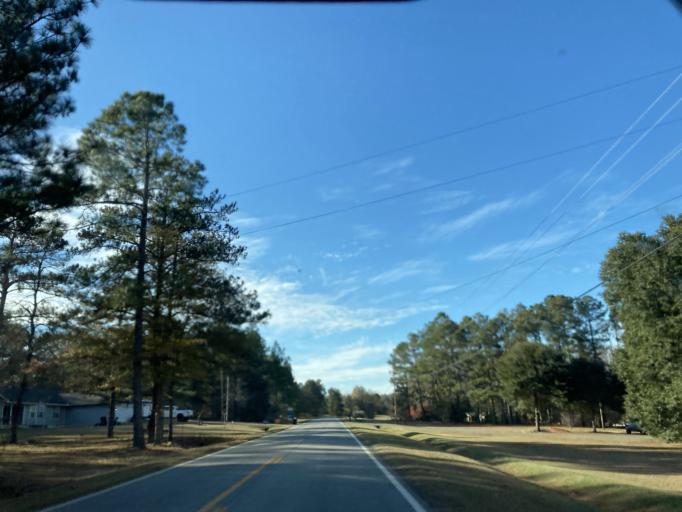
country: US
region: Georgia
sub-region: Jones County
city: Gray
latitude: 32.8969
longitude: -83.5154
